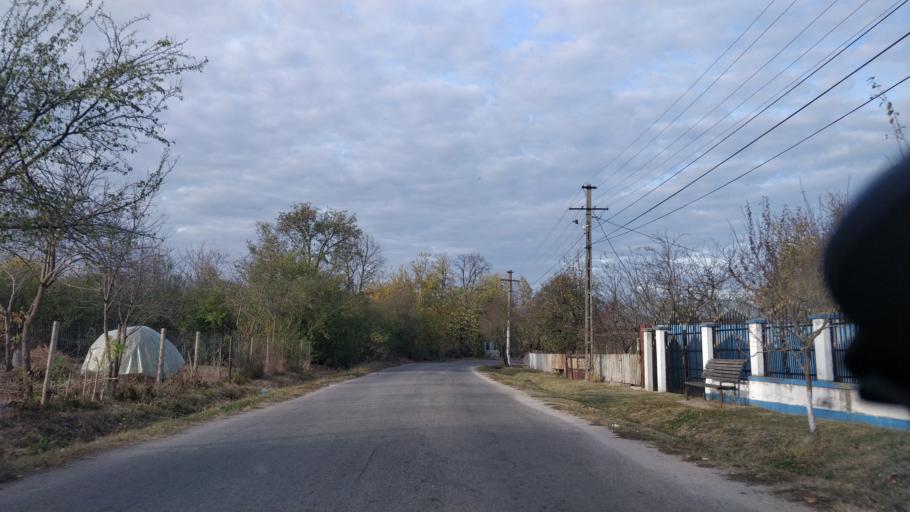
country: RO
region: Giurgiu
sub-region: Comuna Bucsani
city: Bucsani
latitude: 44.3516
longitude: 25.6560
